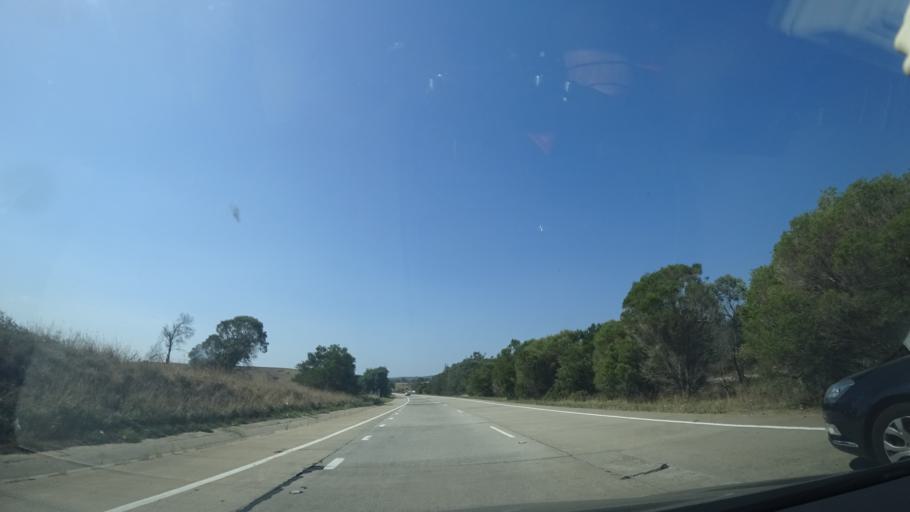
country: AU
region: New South Wales
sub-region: Wingecarribee
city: Moss Vale
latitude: -34.5104
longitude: 150.3080
